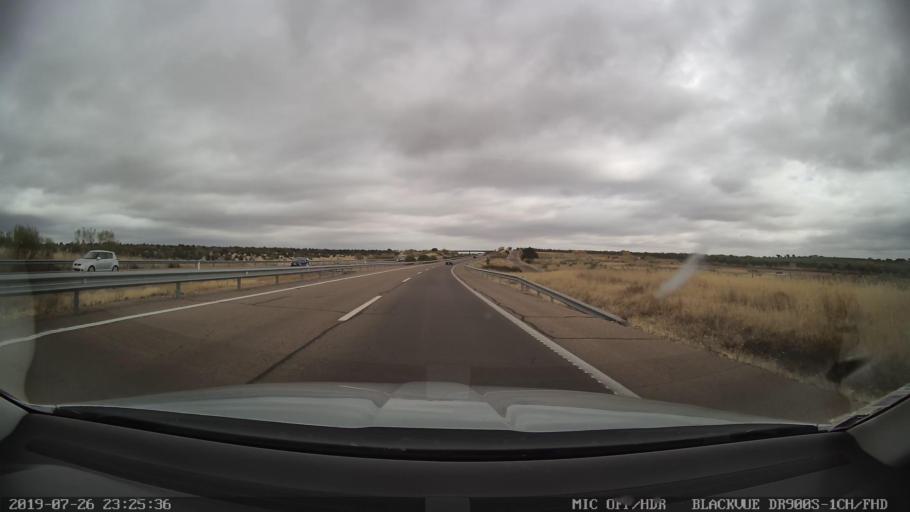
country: ES
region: Extremadura
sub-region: Provincia de Caceres
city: Escurial
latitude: 39.1927
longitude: -5.8887
